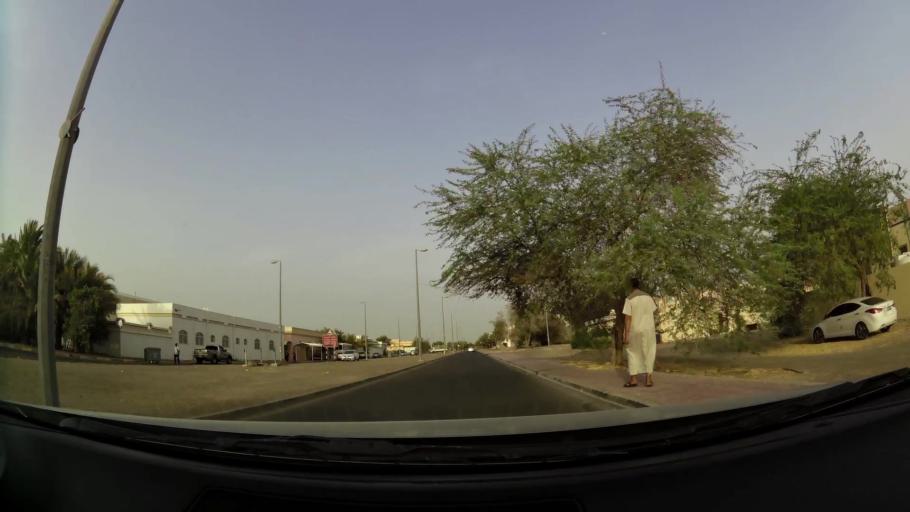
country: OM
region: Al Buraimi
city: Al Buraymi
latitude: 24.2425
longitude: 55.7473
